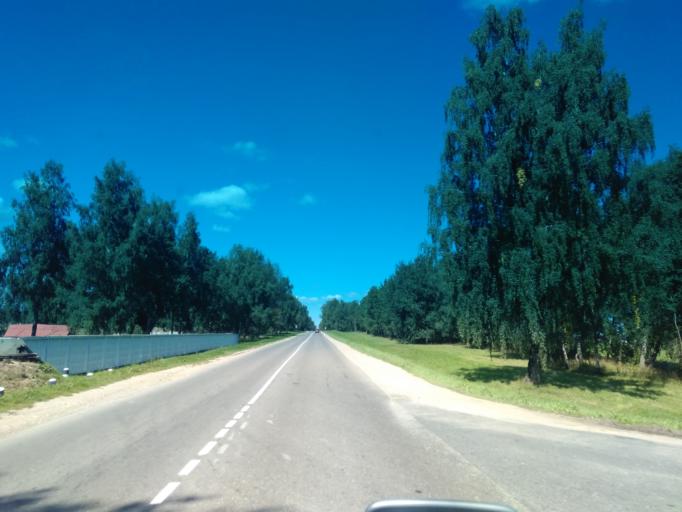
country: BY
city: Fanipol
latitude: 53.7107
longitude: 27.3466
